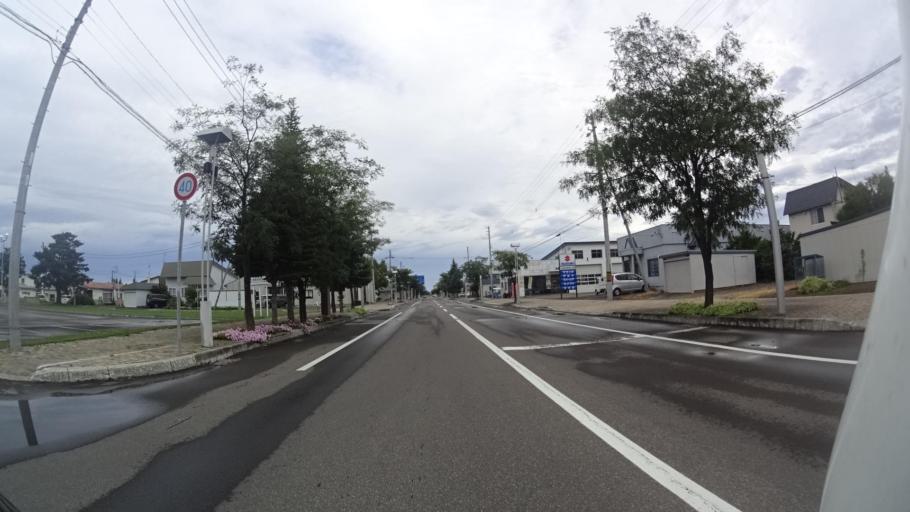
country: JP
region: Hokkaido
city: Abashiri
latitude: 43.8355
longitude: 144.5961
